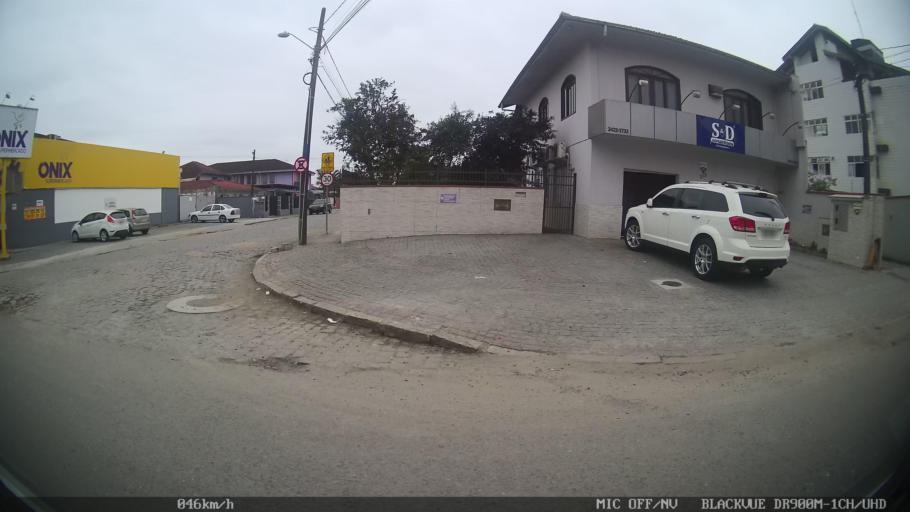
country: BR
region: Santa Catarina
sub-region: Joinville
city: Joinville
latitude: -26.3239
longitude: -48.8301
